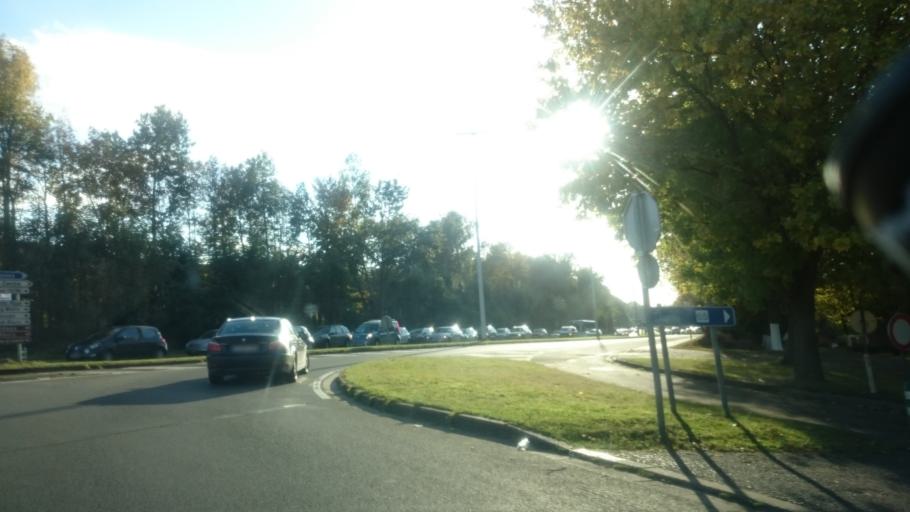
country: BE
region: Wallonia
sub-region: Province du Brabant Wallon
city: Louvain-la-Neuve
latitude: 50.6750
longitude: 4.6118
